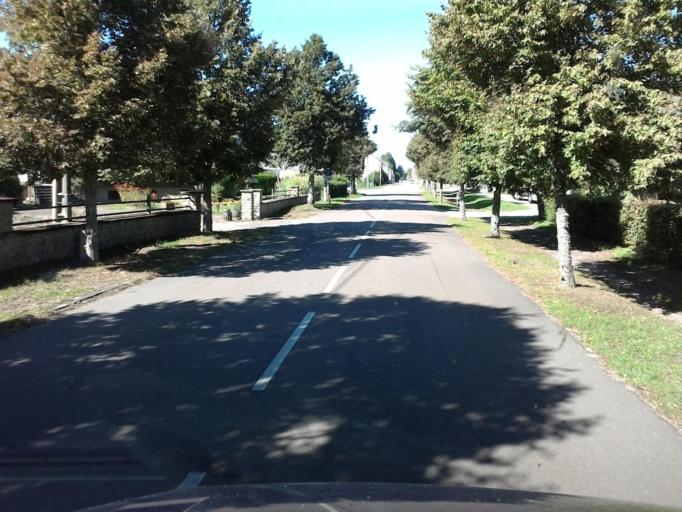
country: FR
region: Bourgogne
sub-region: Departement de la Nievre
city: Lormes
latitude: 47.2809
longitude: 3.8218
